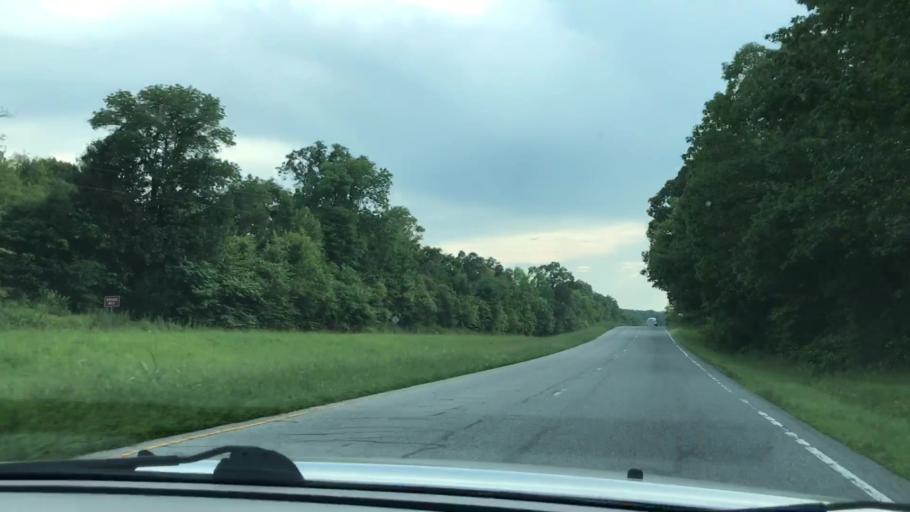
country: US
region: North Carolina
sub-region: Davidson County
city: Denton
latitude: 35.6088
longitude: -80.0214
